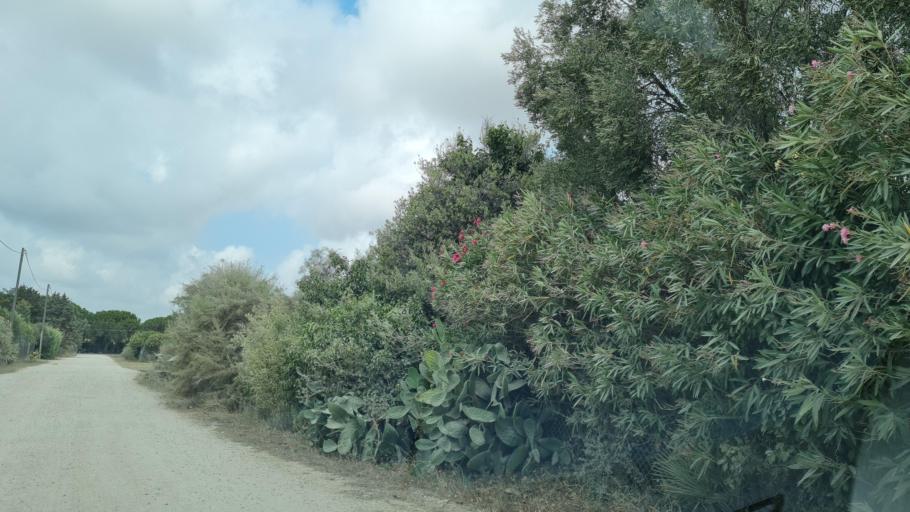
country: IT
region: Latium
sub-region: Provincia di Viterbo
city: Tarquinia
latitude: 42.1929
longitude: 11.7297
